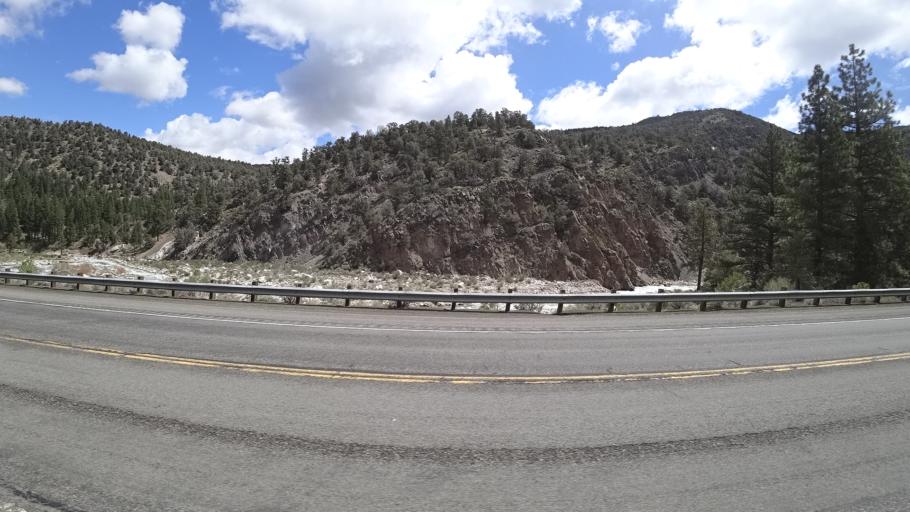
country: US
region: California
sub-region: Mono County
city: Bridgeport
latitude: 38.4286
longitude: -119.4505
